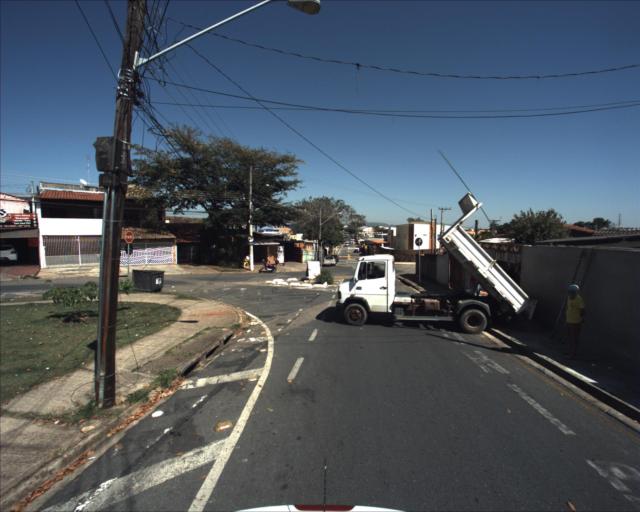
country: BR
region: Sao Paulo
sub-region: Sorocaba
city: Sorocaba
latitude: -23.4702
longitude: -47.4881
